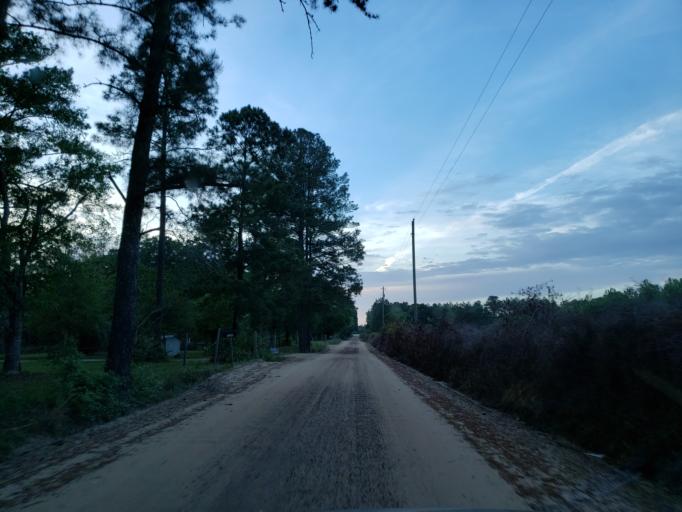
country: US
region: Georgia
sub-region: Lowndes County
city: Hahira
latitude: 30.9701
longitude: -83.3948
